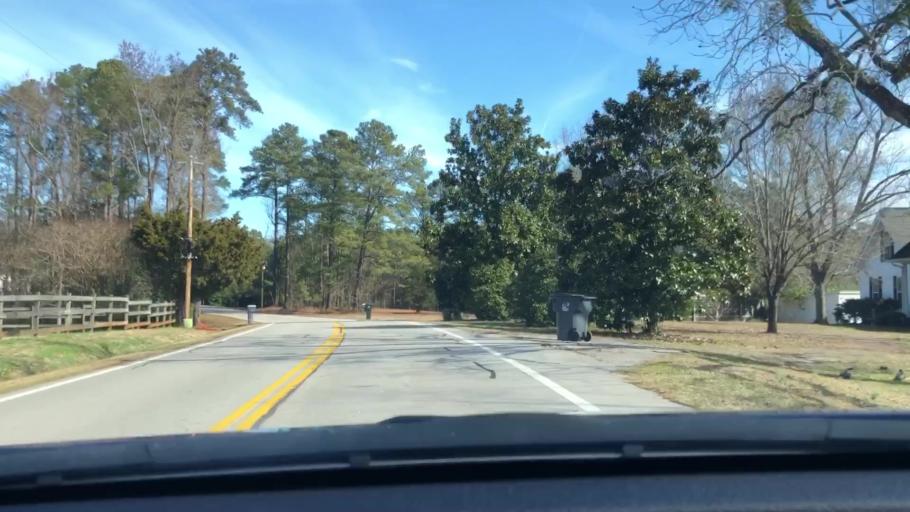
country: US
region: South Carolina
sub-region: Lexington County
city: Irmo
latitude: 34.0565
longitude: -81.1825
